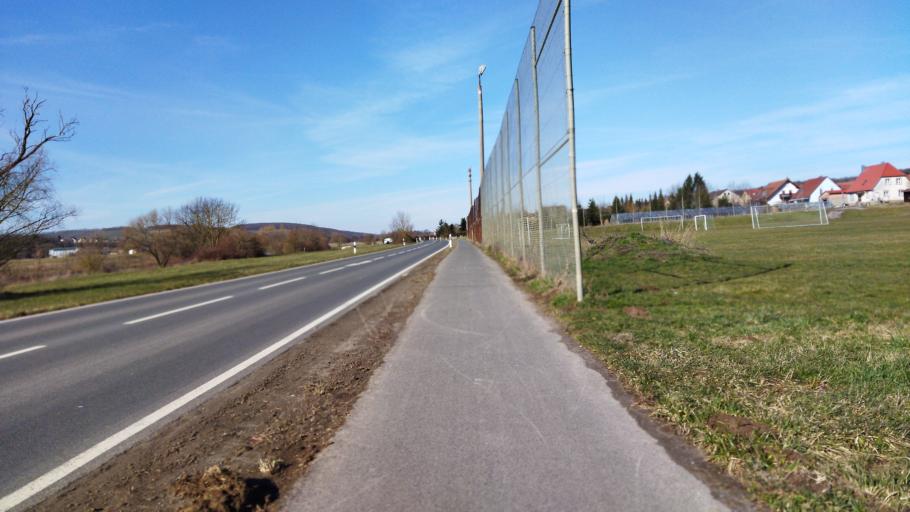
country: DE
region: Bavaria
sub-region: Regierungsbezirk Unterfranken
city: Wipfeld
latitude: 49.9046
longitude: 10.1906
